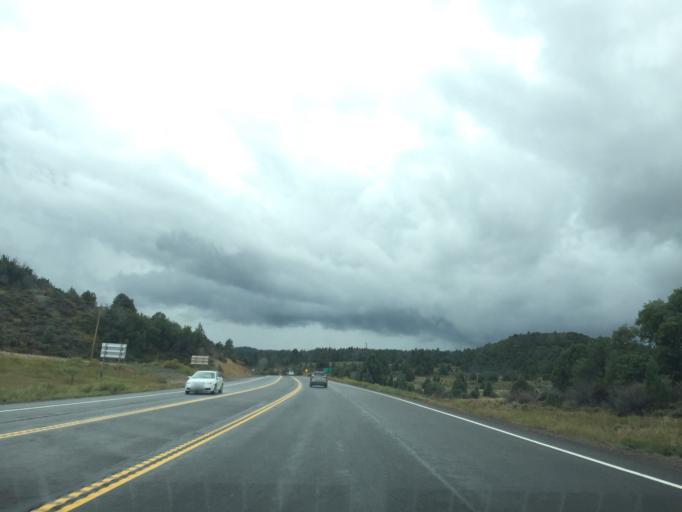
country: US
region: Utah
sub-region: Garfield County
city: Panguitch
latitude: 37.4876
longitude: -112.5132
